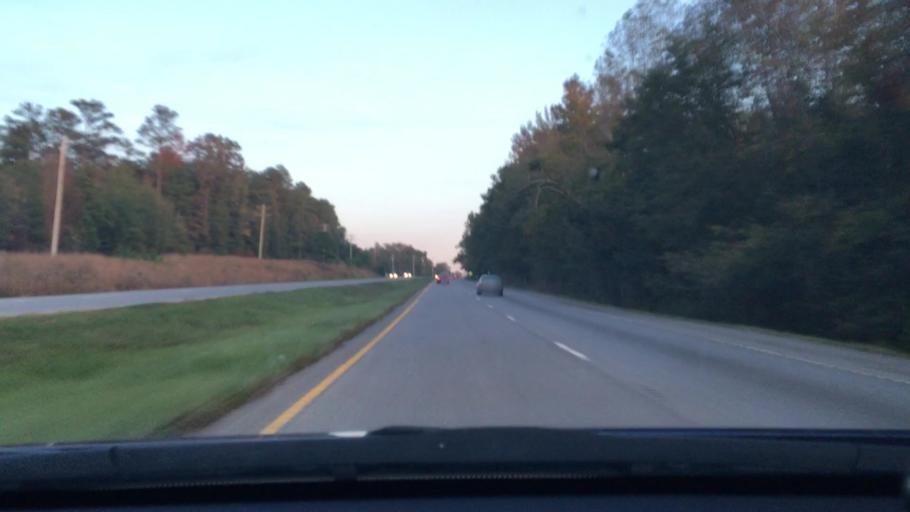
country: US
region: South Carolina
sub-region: Richland County
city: Gadsden
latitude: 33.9425
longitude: -80.7294
